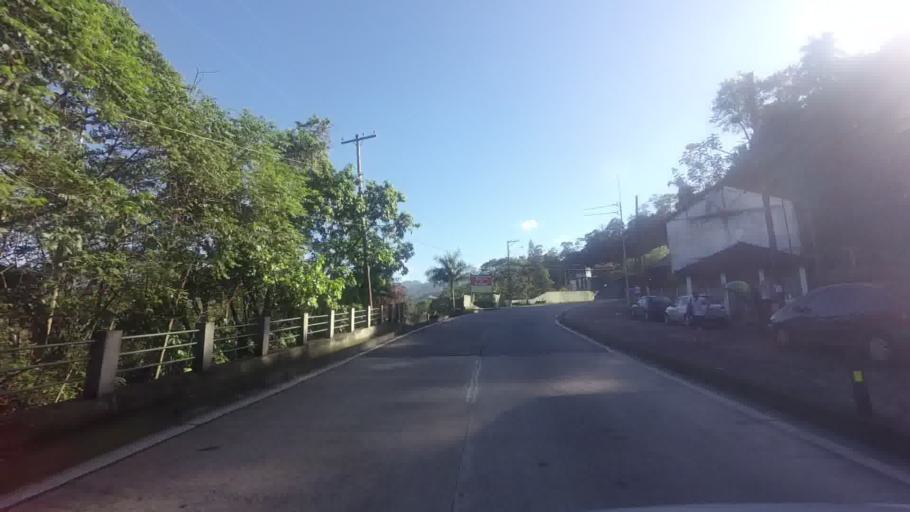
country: BR
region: Rio de Janeiro
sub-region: Petropolis
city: Petropolis
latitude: -22.5704
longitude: -43.2517
